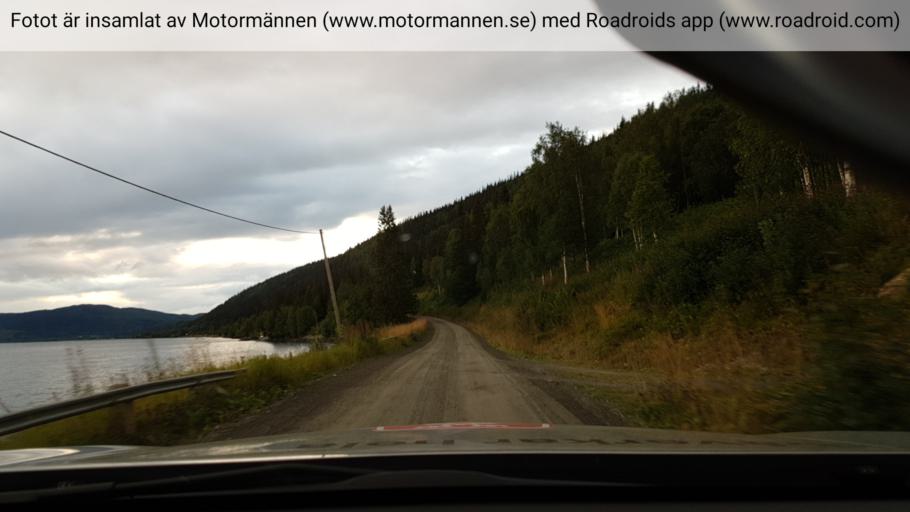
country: NO
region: Nordland
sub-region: Hattfjelldal
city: Hattfjelldal
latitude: 65.6308
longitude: 15.2260
